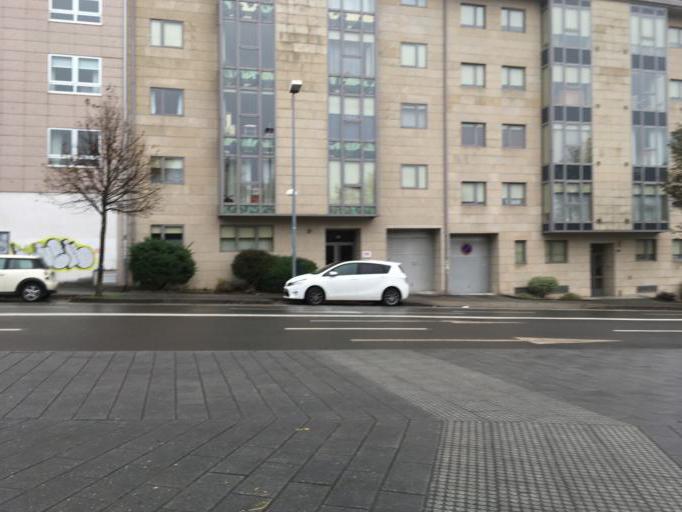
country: ES
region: Galicia
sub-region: Provincia da Coruna
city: Santiago de Compostela
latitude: 42.8695
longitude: -8.5546
